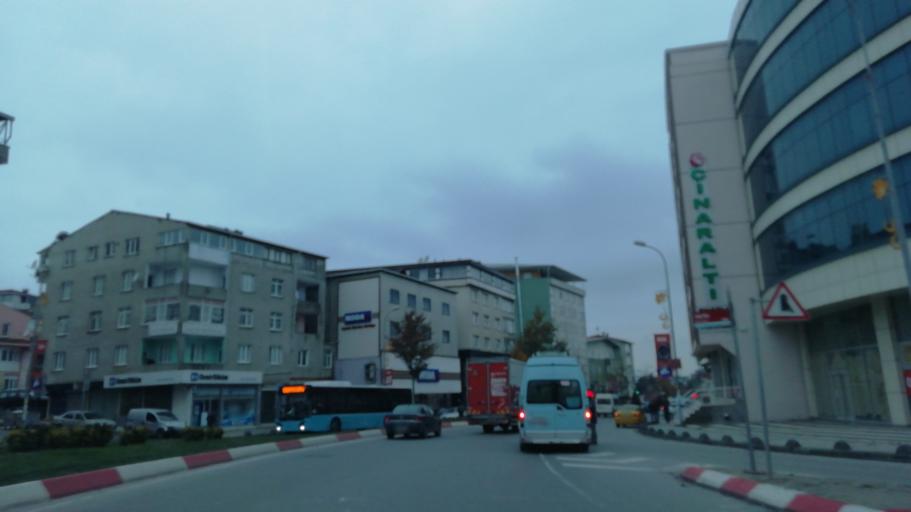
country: TR
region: Istanbul
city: Sultanbeyli
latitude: 40.9704
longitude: 29.2505
